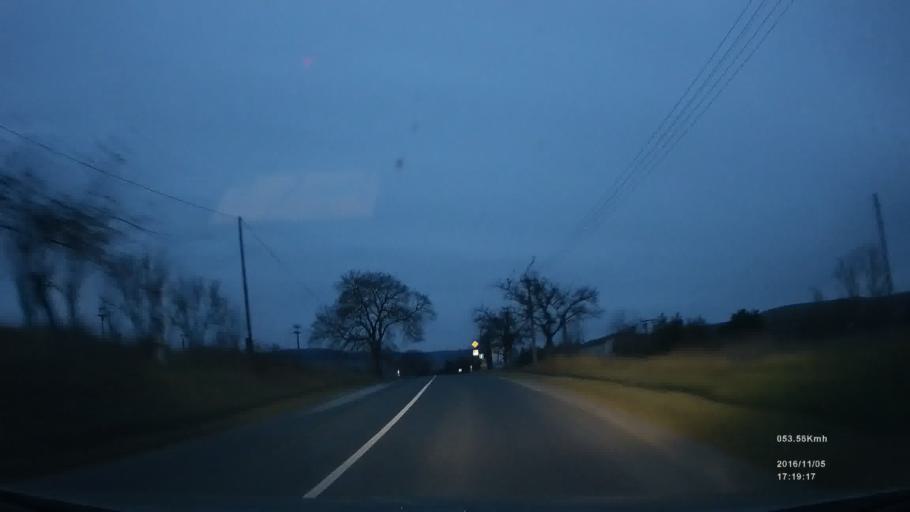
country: SK
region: Presovsky
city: Lubica
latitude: 49.0833
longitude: 20.4267
